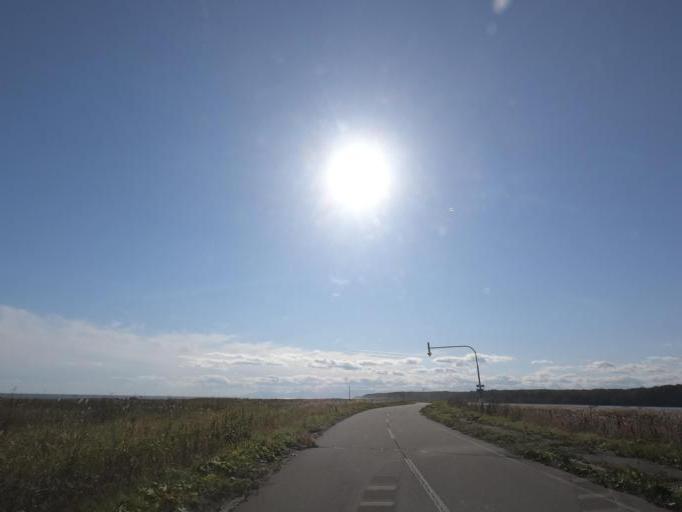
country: JP
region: Hokkaido
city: Obihiro
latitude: 42.5883
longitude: 143.5378
